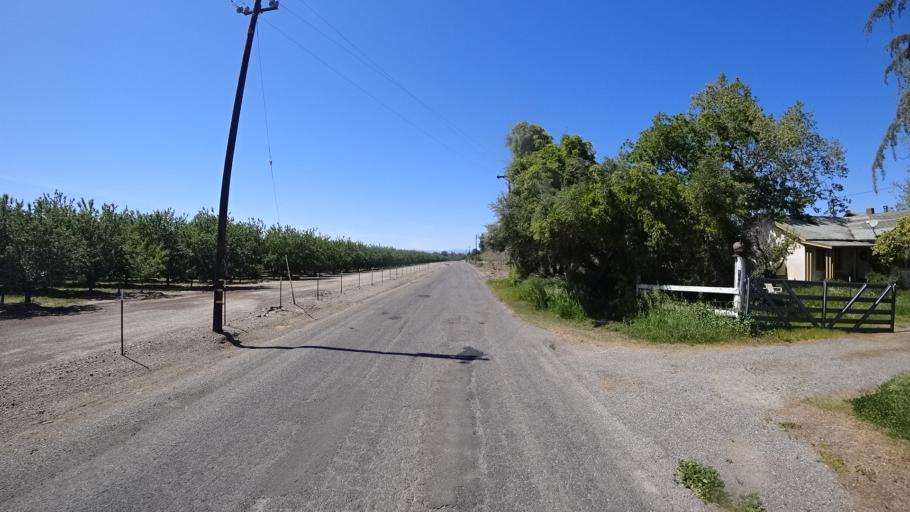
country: US
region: California
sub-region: Glenn County
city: Orland
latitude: 39.7324
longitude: -122.1452
